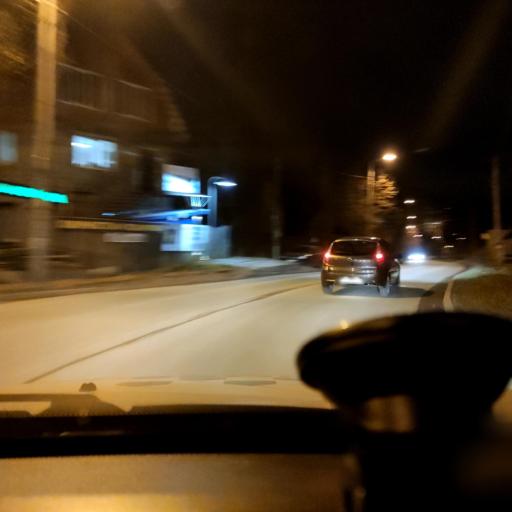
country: RU
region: Perm
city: Perm
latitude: 58.0217
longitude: 56.3128
